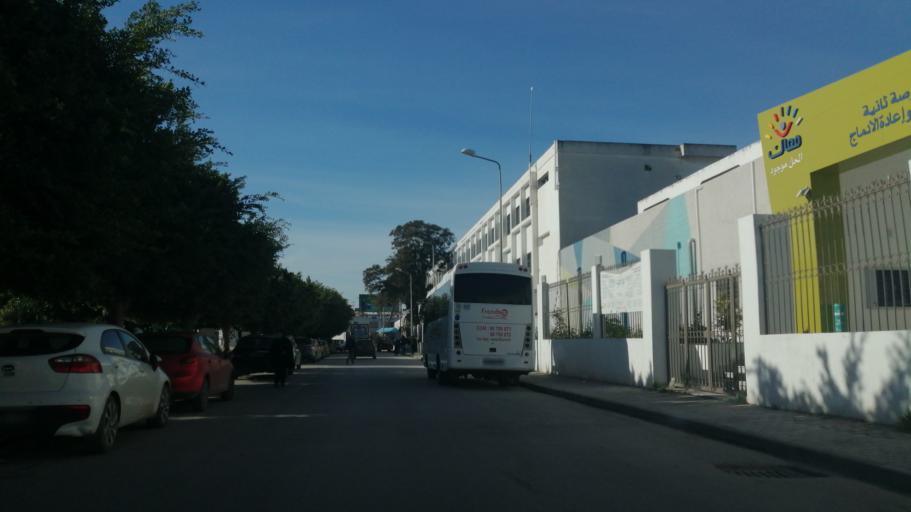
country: TN
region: Tunis
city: Tunis
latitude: 36.8108
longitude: 10.1743
